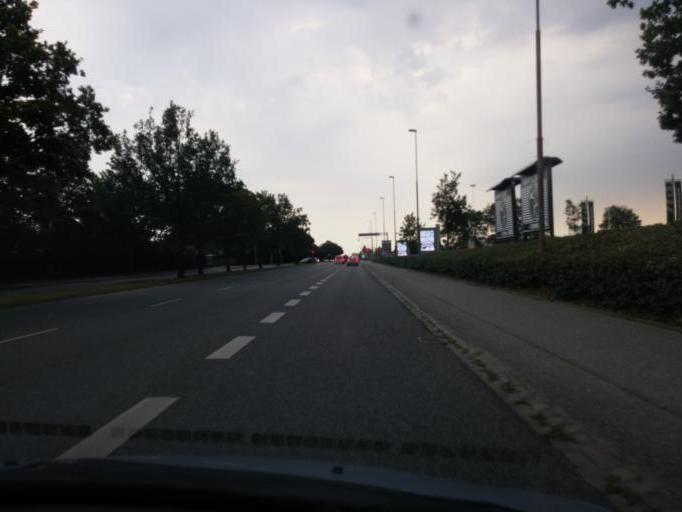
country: DK
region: South Denmark
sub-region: Odense Kommune
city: Neder Holluf
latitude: 55.3860
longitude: 10.4278
